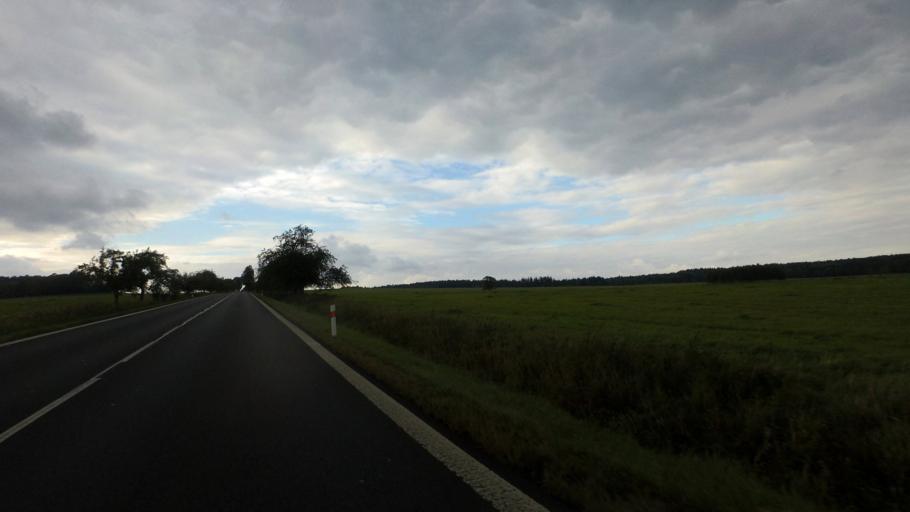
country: CZ
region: Ustecky
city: Stare Krecany
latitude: 50.9671
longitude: 14.5248
